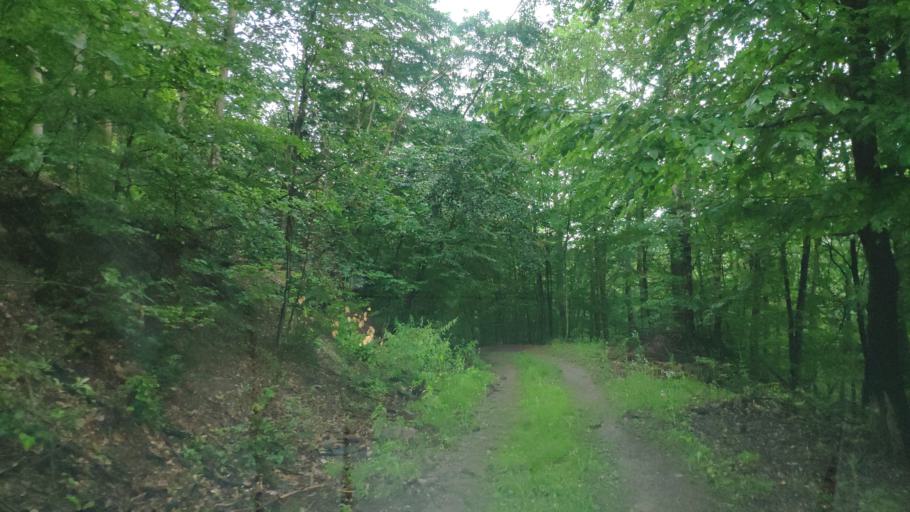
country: SK
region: Presovsky
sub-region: Okres Presov
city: Presov
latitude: 48.8673
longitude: 21.2102
